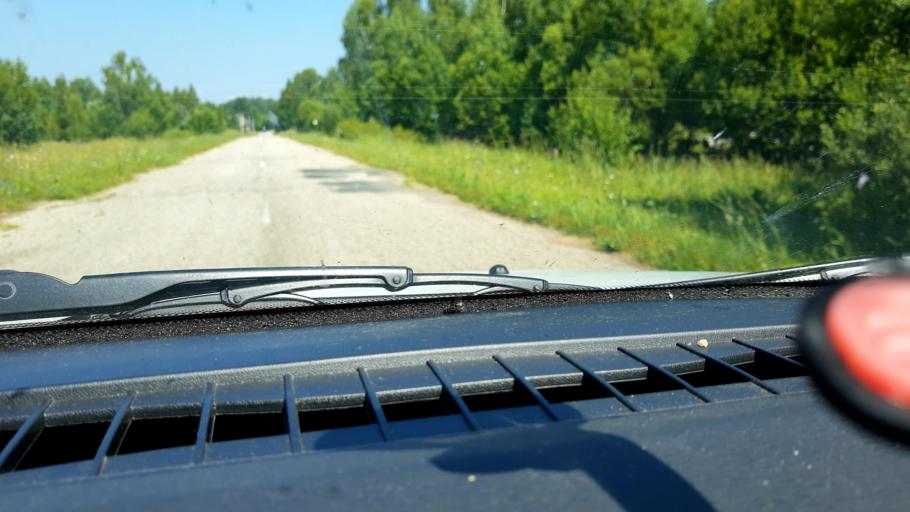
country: RU
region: Nizjnij Novgorod
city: Sharanga
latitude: 57.0340
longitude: 46.7219
